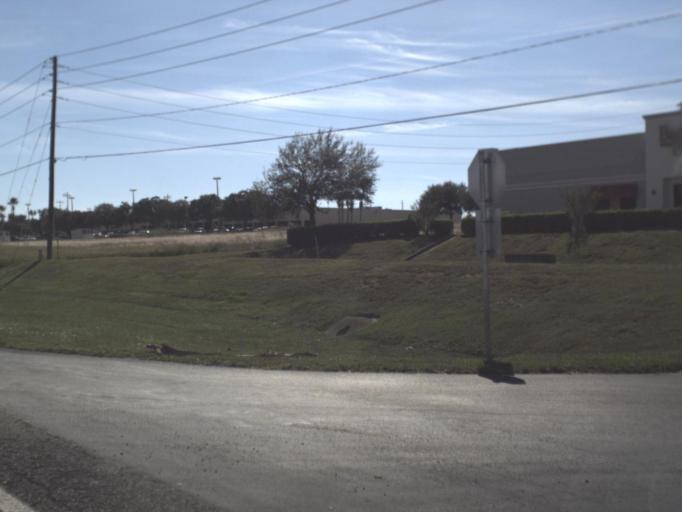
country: US
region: Florida
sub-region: Highlands County
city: Lake Placid
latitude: 27.3041
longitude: -81.3587
